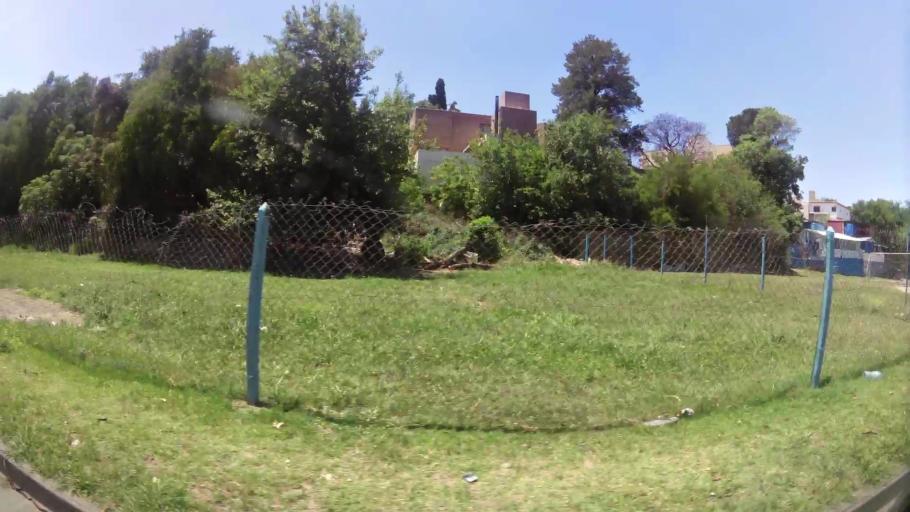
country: AR
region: Cordoba
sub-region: Departamento de Capital
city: Cordoba
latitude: -31.4021
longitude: -64.2035
